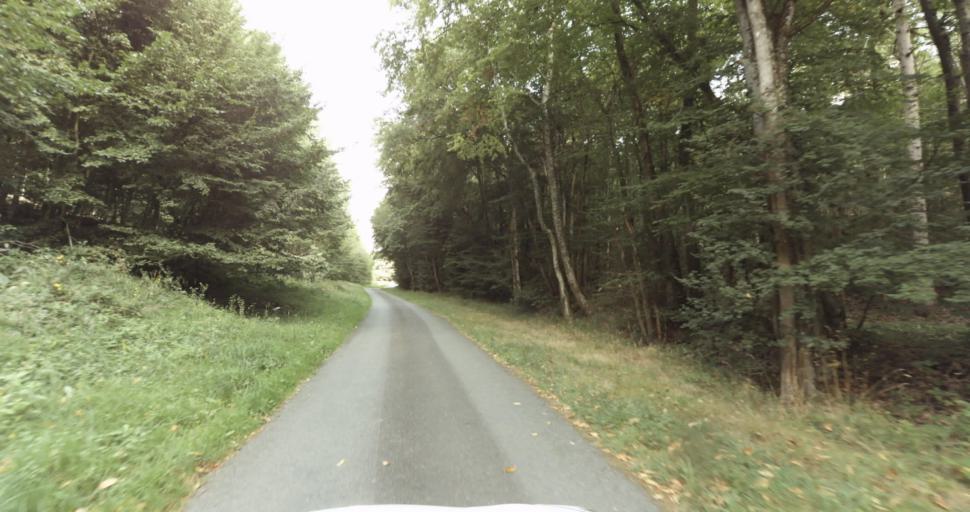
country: FR
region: Haute-Normandie
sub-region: Departement de l'Eure
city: Tillieres-sur-Avre
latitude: 48.7725
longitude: 1.1078
